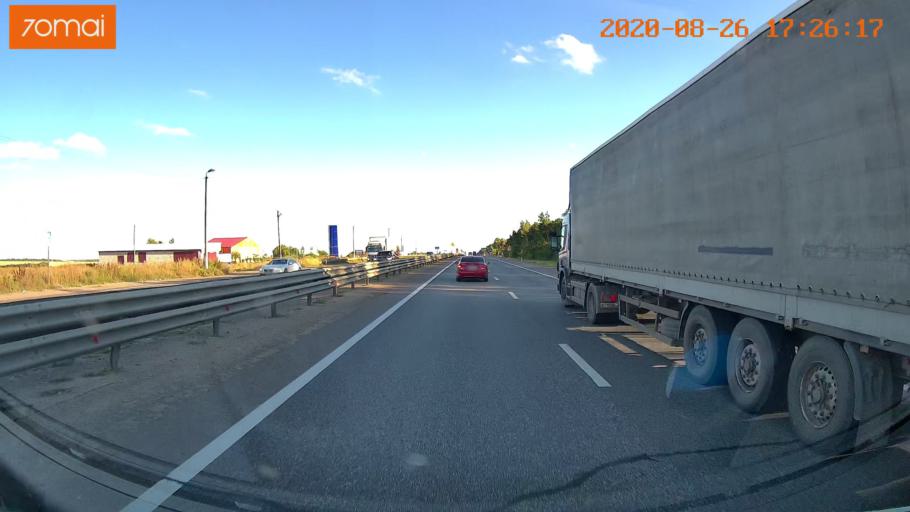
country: RU
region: Tula
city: Volovo
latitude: 53.4889
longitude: 38.1159
